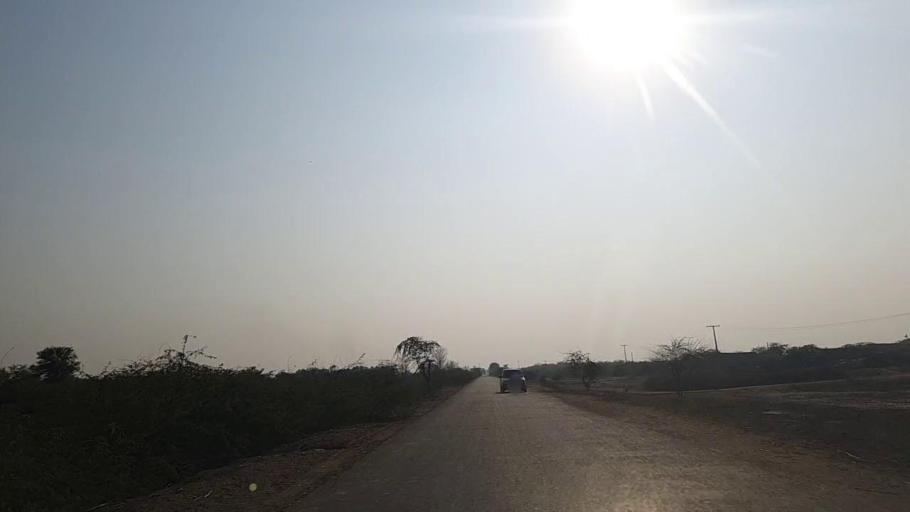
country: PK
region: Sindh
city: Jam Sahib
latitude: 26.2682
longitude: 68.6095
